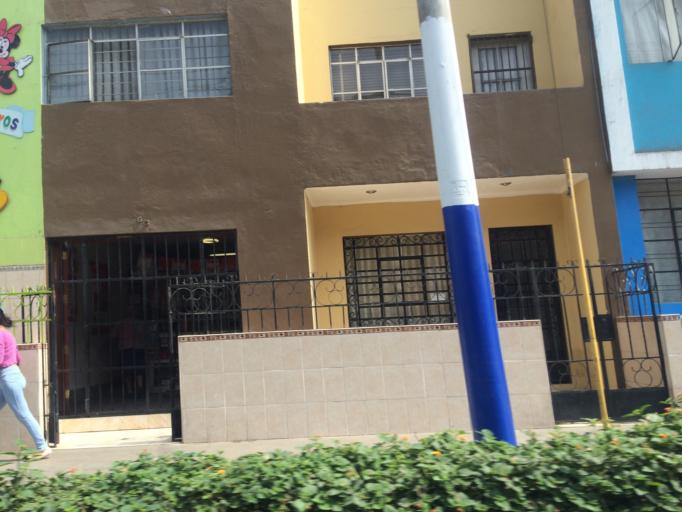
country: PE
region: Lima
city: Lima
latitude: -12.0282
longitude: -77.0351
